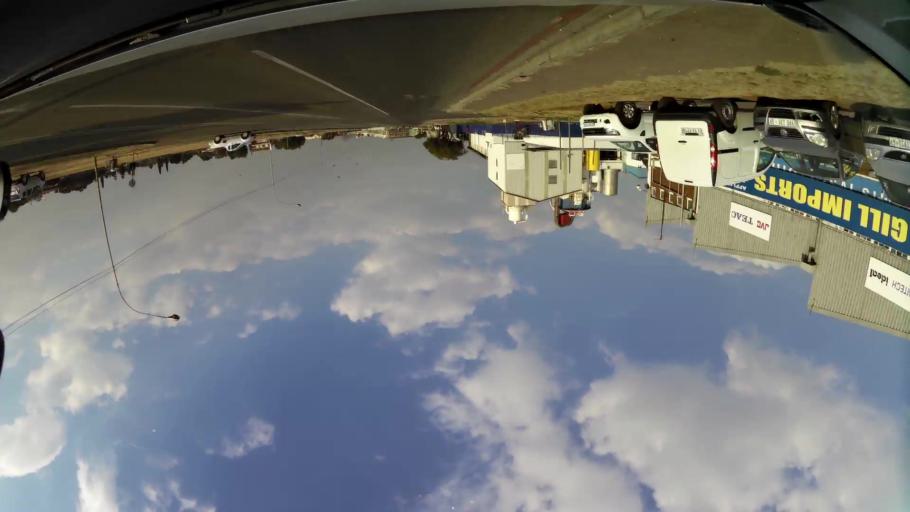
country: ZA
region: Gauteng
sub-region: City of Johannesburg Metropolitan Municipality
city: Modderfontein
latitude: -26.1126
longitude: 28.2090
